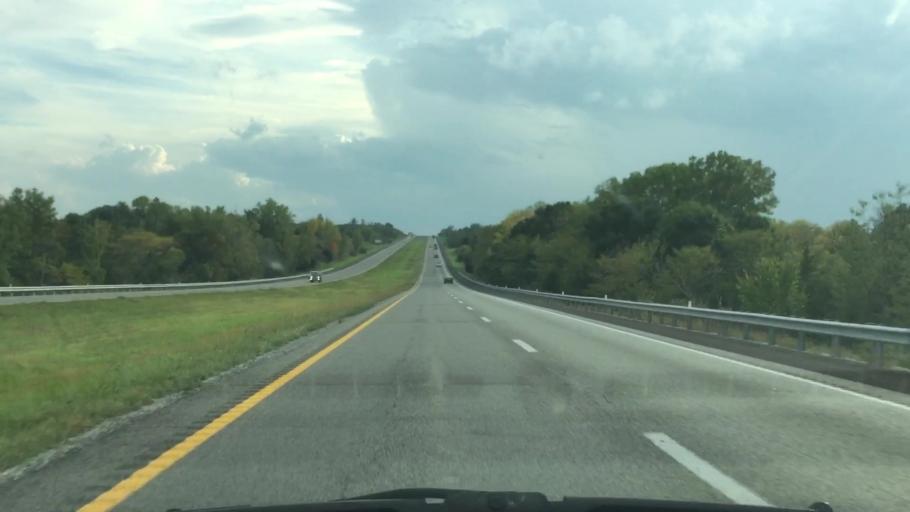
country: US
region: Missouri
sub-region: Daviess County
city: Gallatin
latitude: 39.9159
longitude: -94.1429
